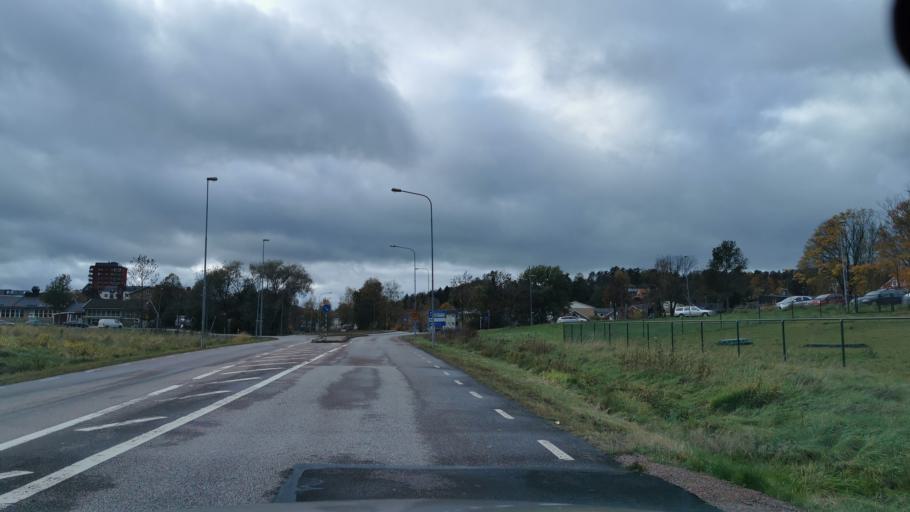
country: SE
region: Vaestra Goetaland
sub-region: Partille Kommun
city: Partille
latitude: 57.7227
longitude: 12.0798
